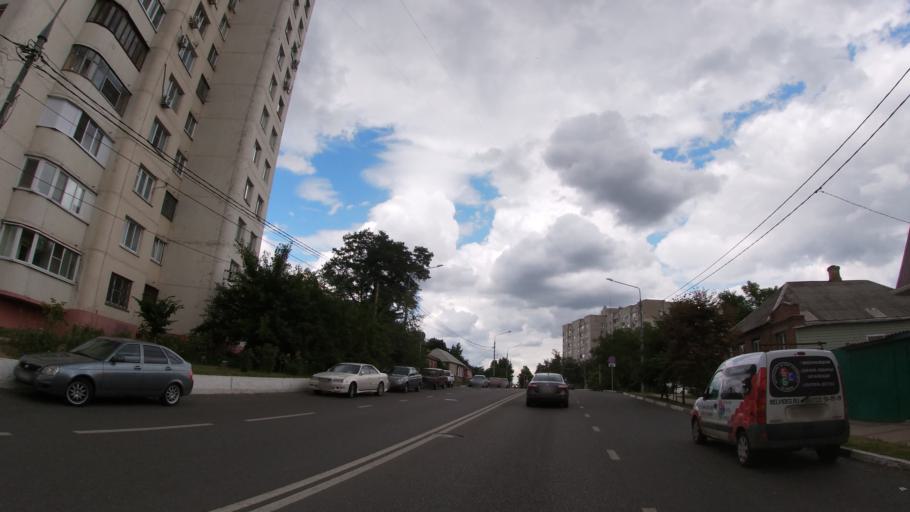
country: RU
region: Belgorod
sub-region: Belgorodskiy Rayon
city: Belgorod
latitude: 50.6010
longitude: 36.6086
